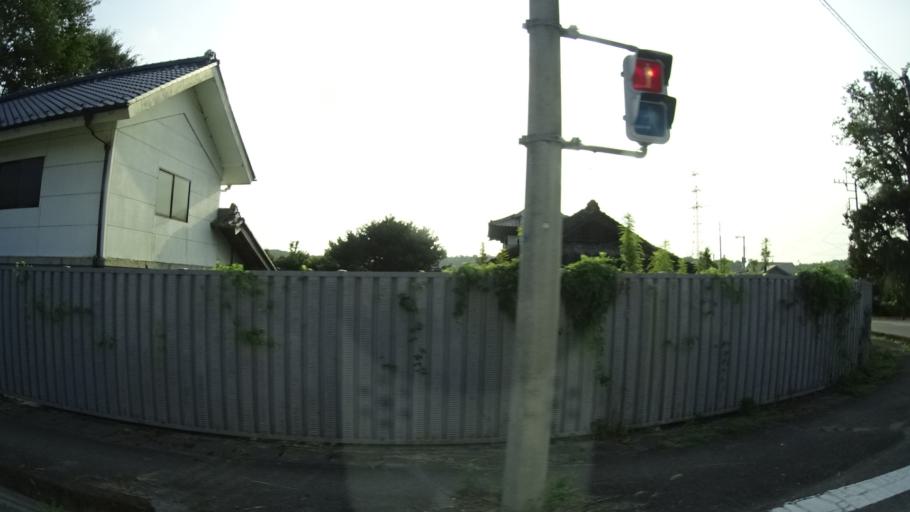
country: JP
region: Tochigi
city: Motegi
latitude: 36.5627
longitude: 140.1030
